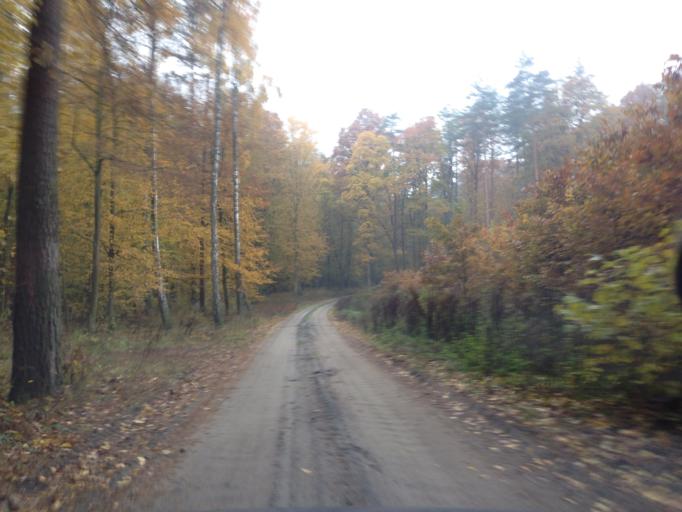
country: PL
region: Kujawsko-Pomorskie
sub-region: Powiat brodnicki
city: Gorzno
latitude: 53.2135
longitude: 19.6860
